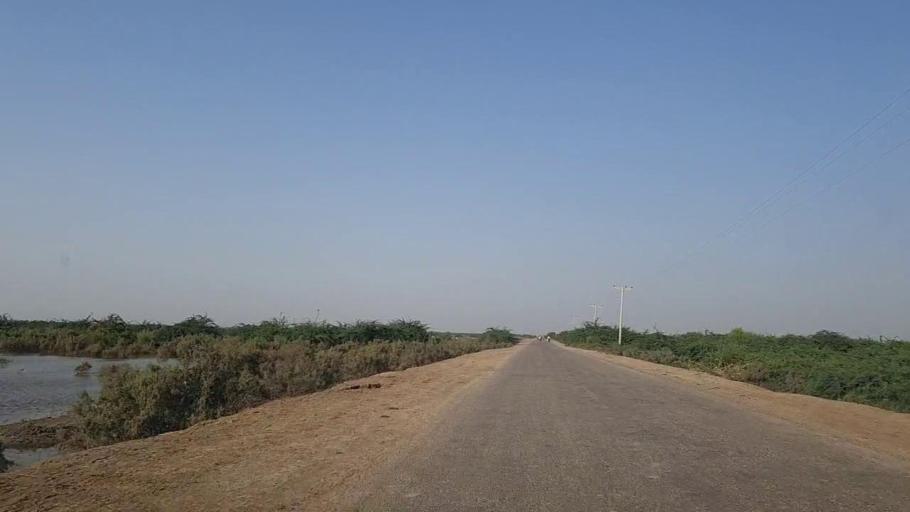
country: PK
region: Sindh
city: Mirpur Batoro
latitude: 24.6042
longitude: 68.4016
